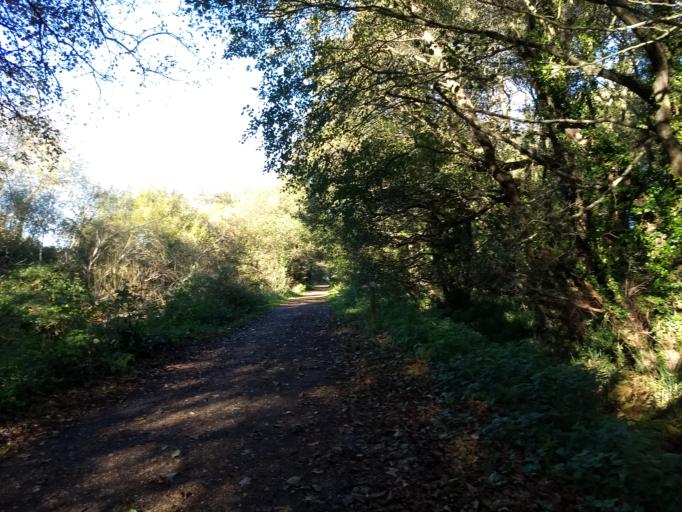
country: GB
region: England
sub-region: Isle of Wight
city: Newport
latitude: 50.6811
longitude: -1.2899
